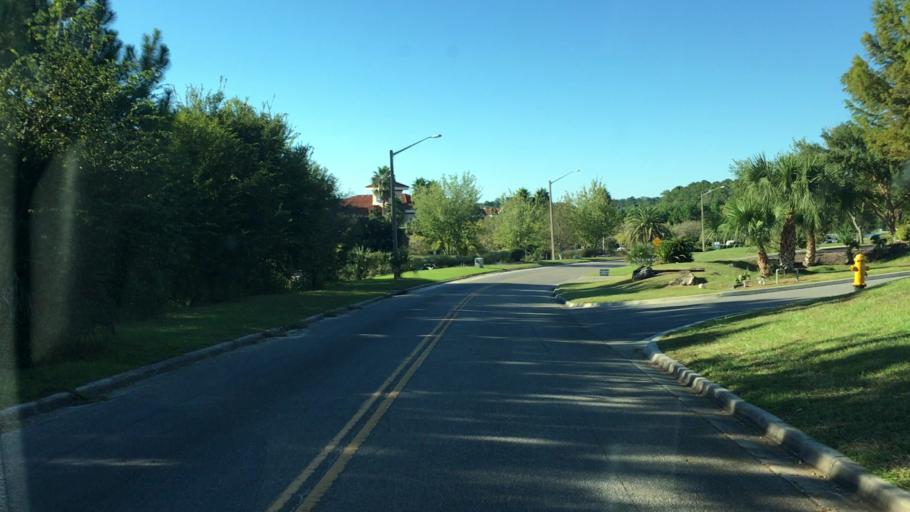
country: US
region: Florida
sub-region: Alachua County
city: Alachua
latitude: 29.6907
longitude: -82.4508
